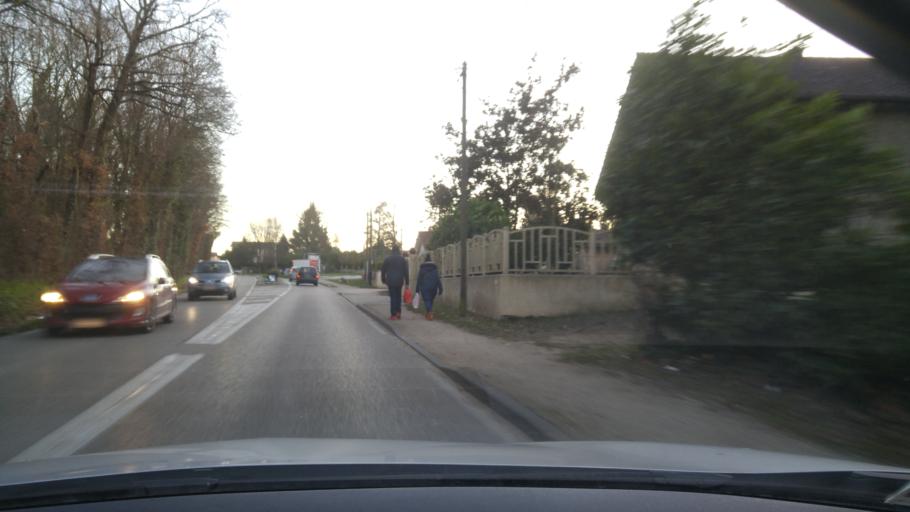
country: FR
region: Rhone-Alpes
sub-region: Departement de l'Isere
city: Tignieu-Jameyzieu
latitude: 45.7410
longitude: 5.1872
